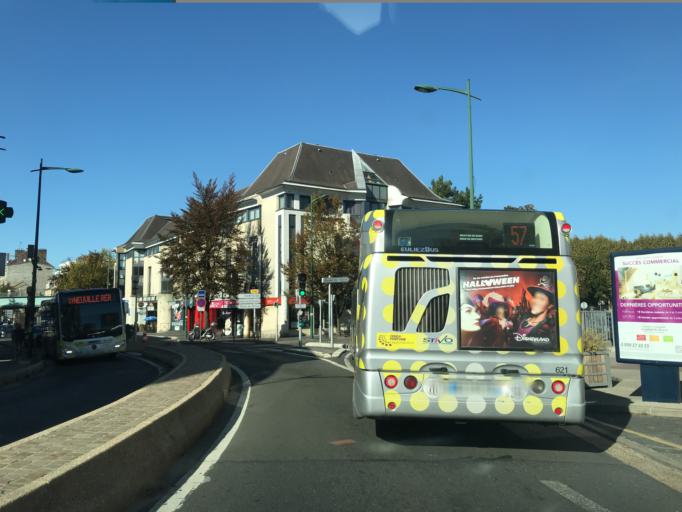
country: FR
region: Ile-de-France
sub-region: Departement du Val-d'Oise
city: Pontoise
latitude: 49.0444
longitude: 2.1080
